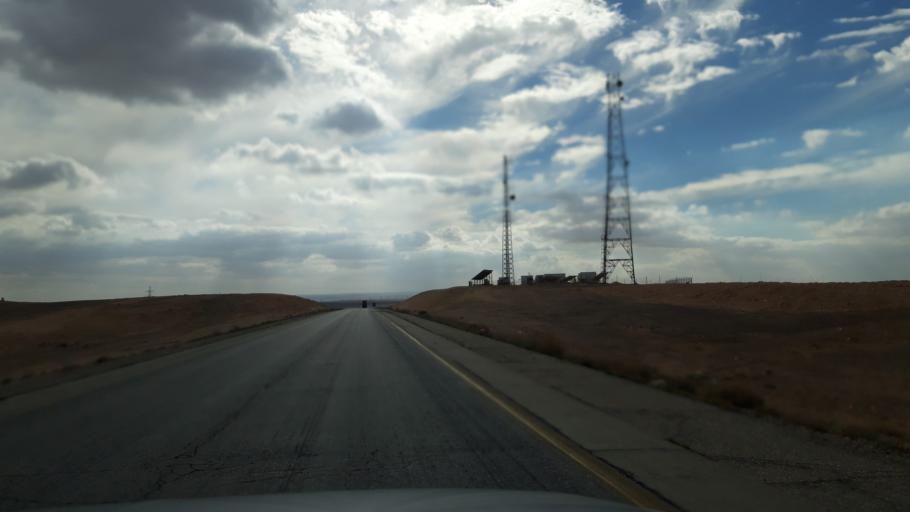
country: JO
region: Amman
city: Al Azraq ash Shamali
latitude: 31.7373
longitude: 36.5214
